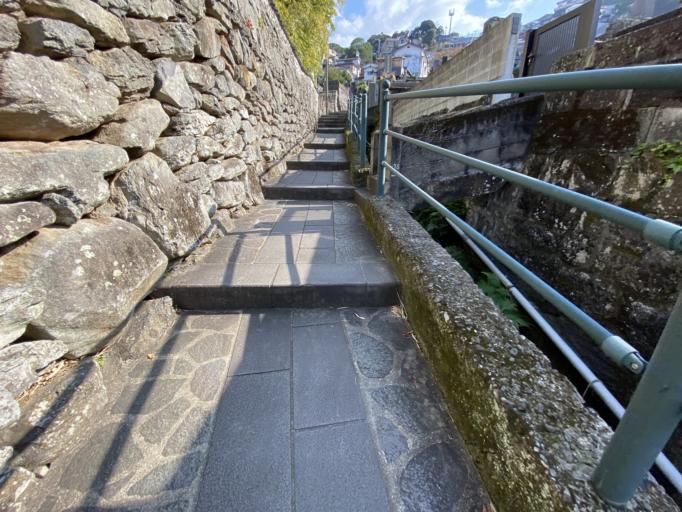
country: JP
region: Nagasaki
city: Nagasaki-shi
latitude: 32.7497
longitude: 129.8852
